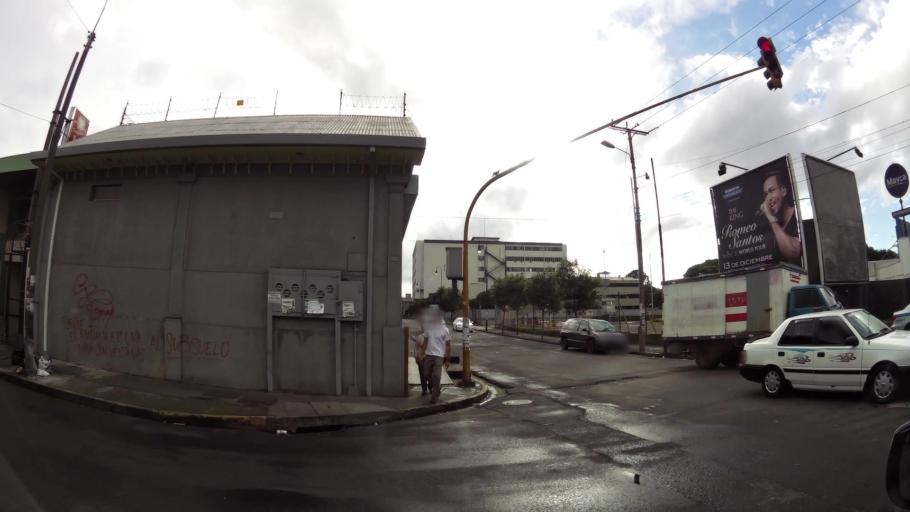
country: CR
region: San Jose
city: San Jose
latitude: 9.9356
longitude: -84.0874
